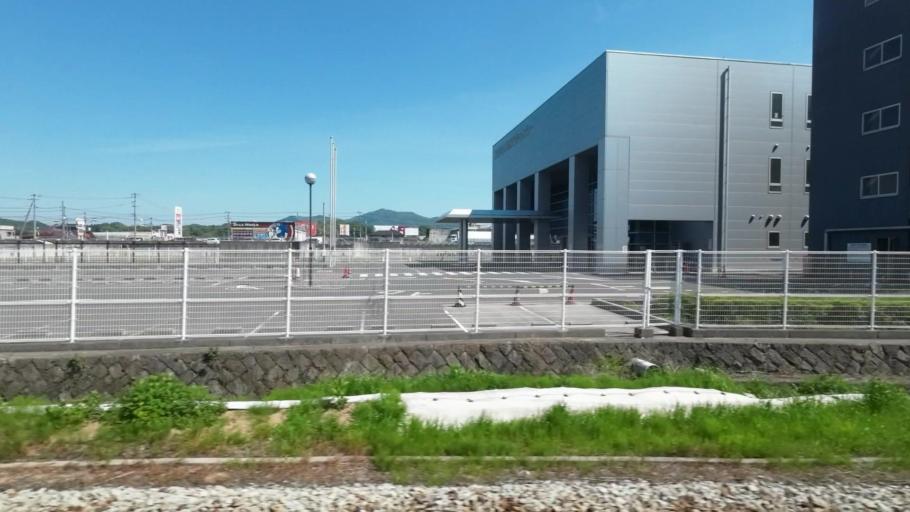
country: JP
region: Hiroshima
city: Fukuyama
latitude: 34.4770
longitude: 133.3142
